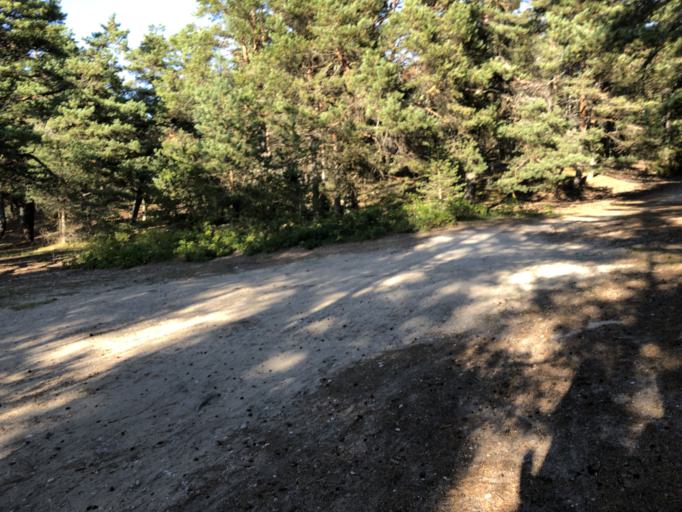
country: EE
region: Harju
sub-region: Paldiski linn
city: Paldiski
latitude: 59.3708
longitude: 24.2388
